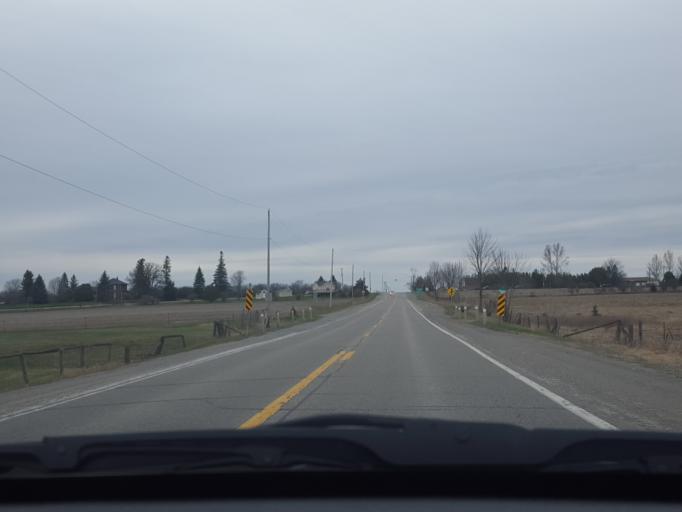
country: CA
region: Ontario
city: Uxbridge
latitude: 44.3151
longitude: -79.1790
